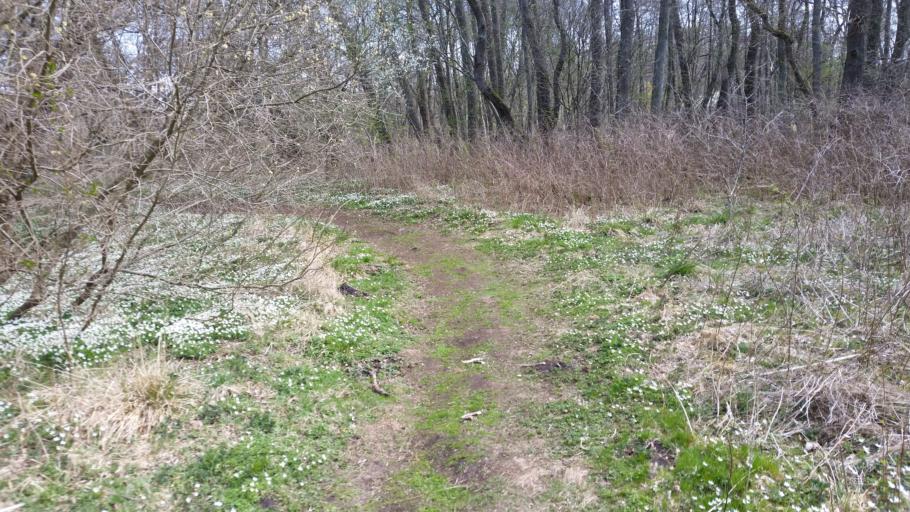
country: DK
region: Capital Region
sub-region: Helsingor Kommune
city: Hornbaek
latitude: 56.0751
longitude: 12.4086
